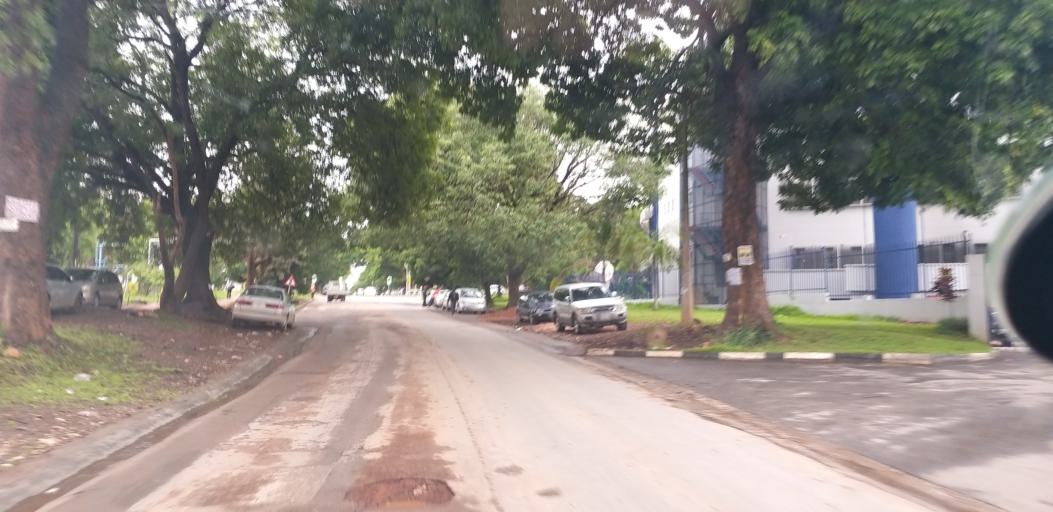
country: ZM
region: Lusaka
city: Lusaka
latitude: -15.4191
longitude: 28.2999
